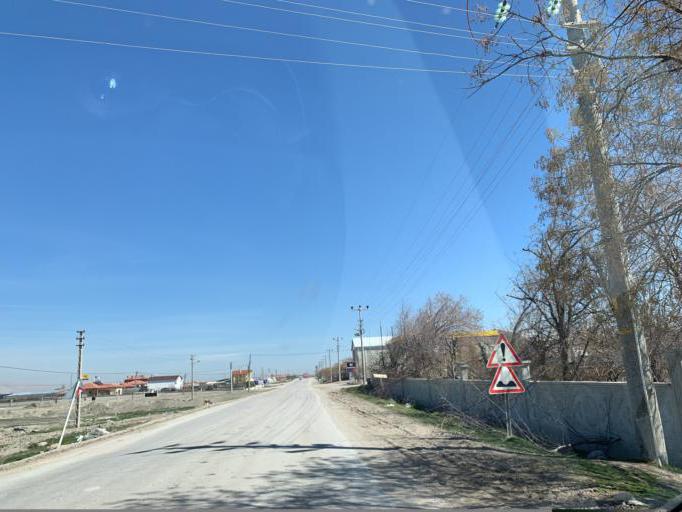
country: TR
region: Konya
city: Yarma
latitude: 37.7495
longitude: 32.8433
